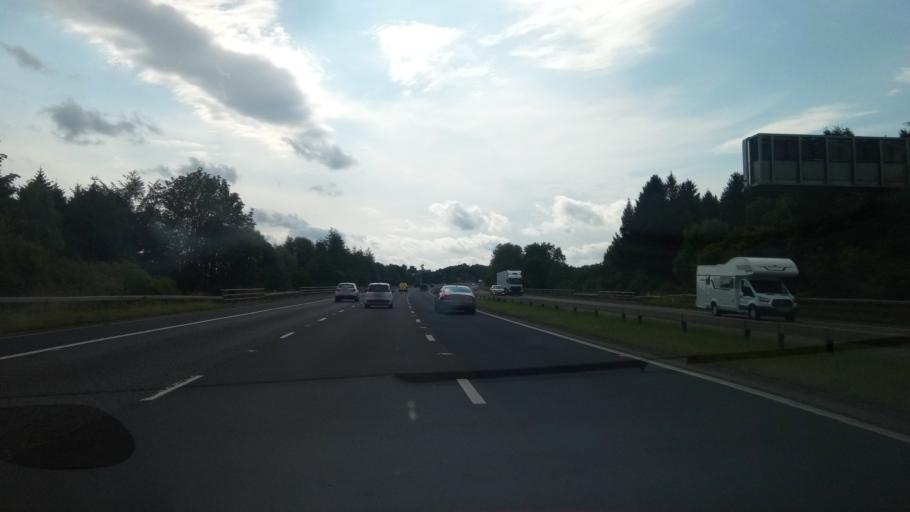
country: GB
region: England
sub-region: Cumbria
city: Penrith
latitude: 54.6437
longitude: -2.7384
